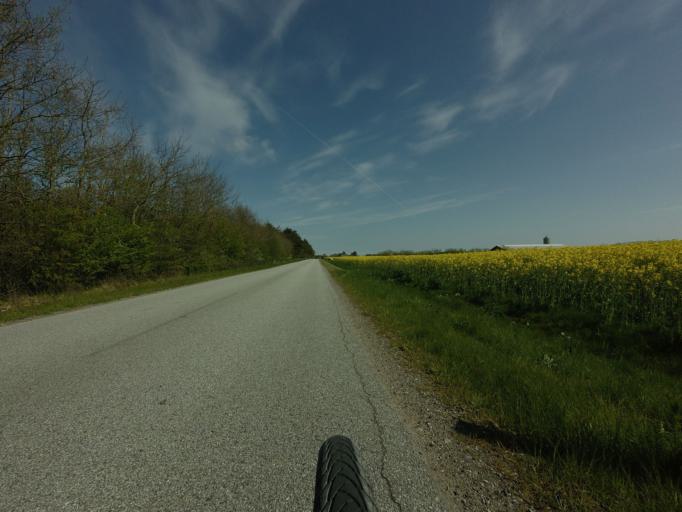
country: DK
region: North Denmark
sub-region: Jammerbugt Kommune
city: Pandrup
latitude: 57.2290
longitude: 9.6130
